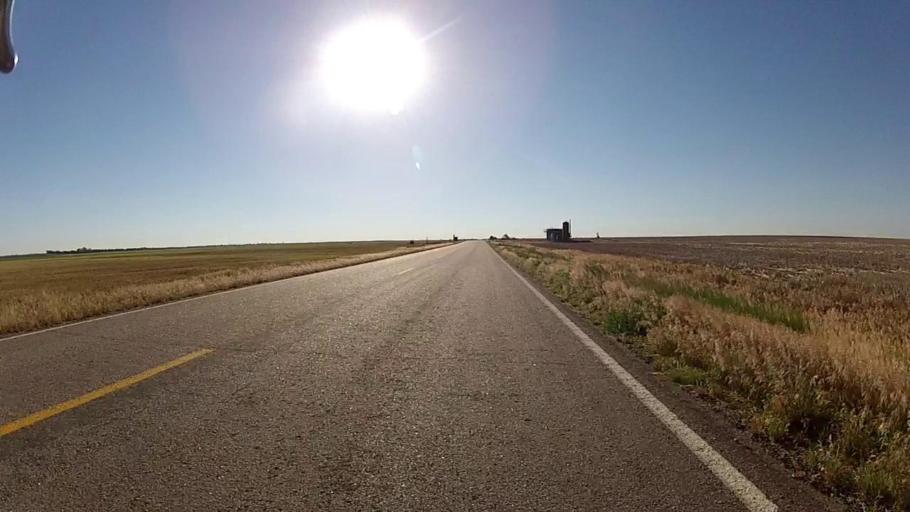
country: US
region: Kansas
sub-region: Ford County
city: Dodge City
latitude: 37.6461
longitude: -99.8260
